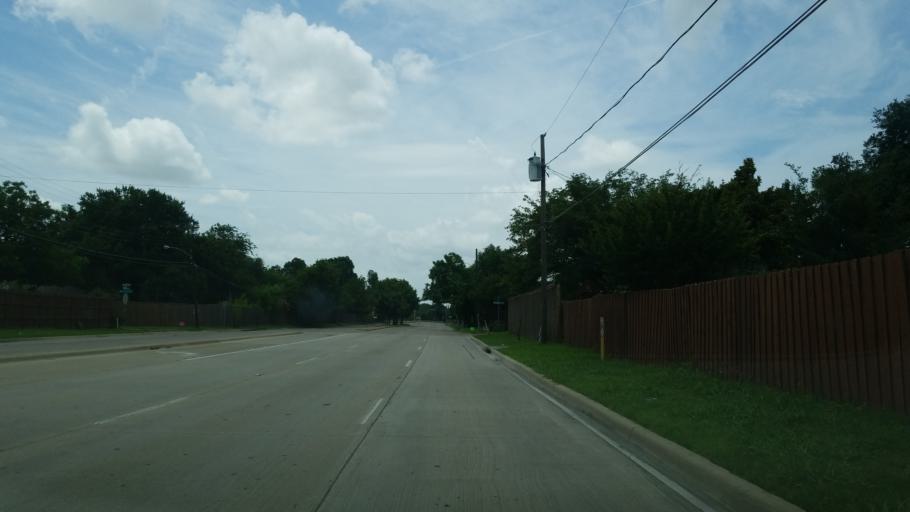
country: US
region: Texas
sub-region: Dallas County
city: Farmers Branch
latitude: 32.8901
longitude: -96.8705
